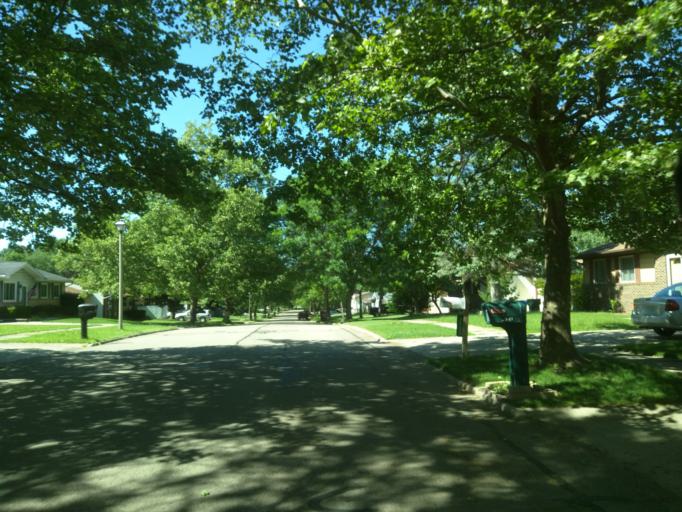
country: US
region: Michigan
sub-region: Ingham County
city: Edgemont Park
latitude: 42.7578
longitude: -84.5935
